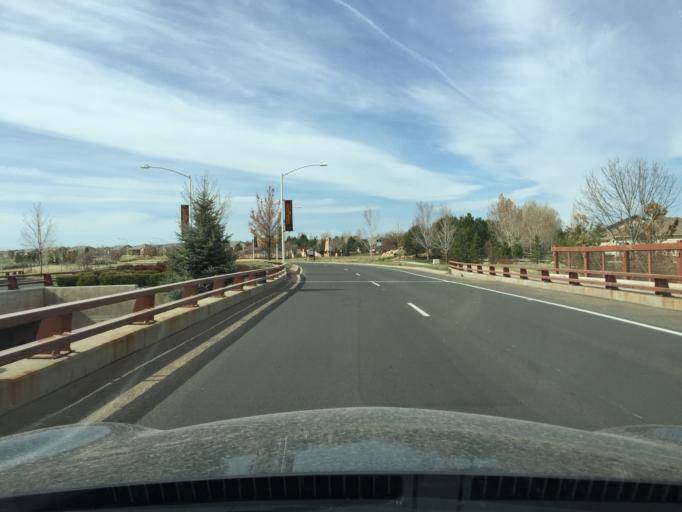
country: US
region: Colorado
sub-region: Boulder County
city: Lafayette
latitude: 39.9981
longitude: -105.0381
